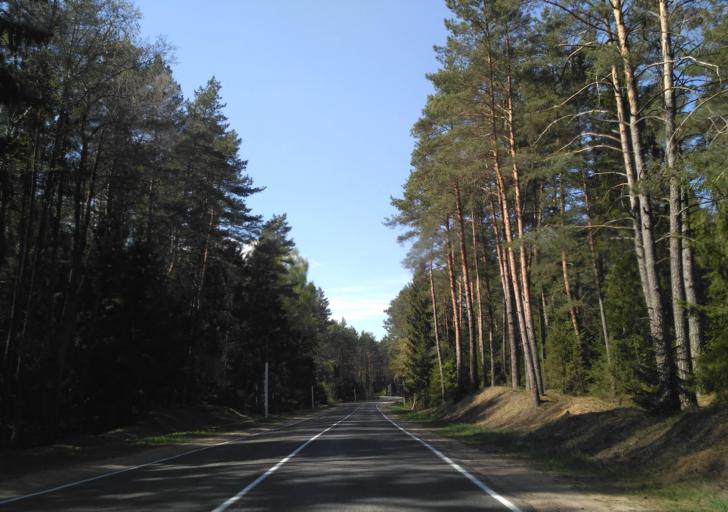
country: BY
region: Minsk
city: Narach
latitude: 54.9096
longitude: 26.7280
